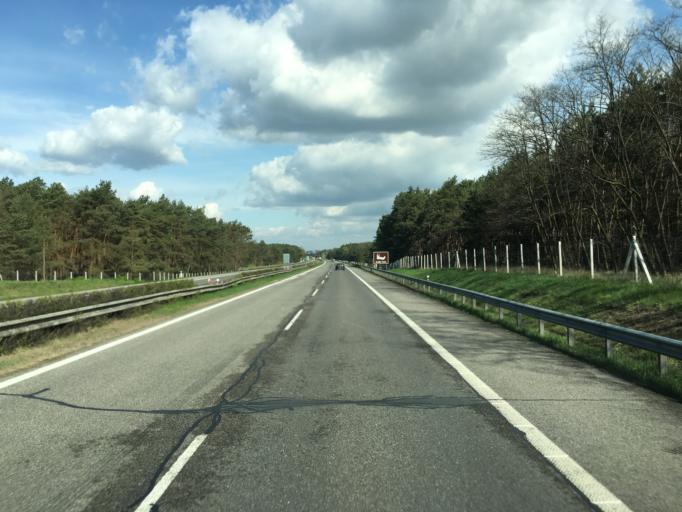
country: CZ
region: South Moravian
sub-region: Okres Breclav
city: Lanzhot
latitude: 48.6171
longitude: 17.0122
